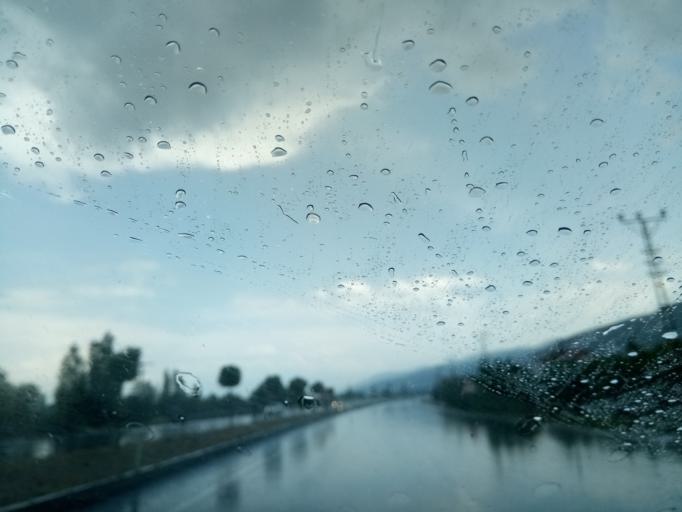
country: TR
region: Afyonkarahisar
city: Sultandagi
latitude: 38.4929
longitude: 31.2735
